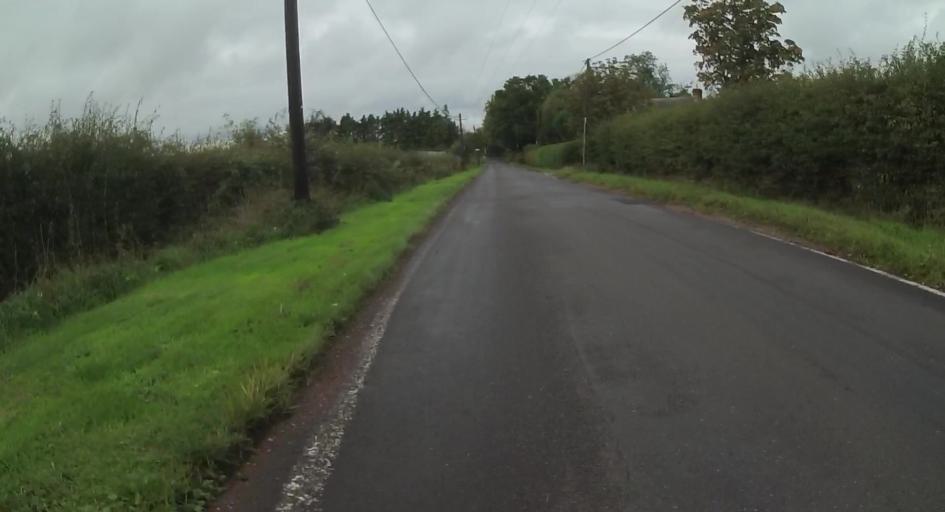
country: GB
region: England
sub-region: Hampshire
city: Tadley
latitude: 51.3155
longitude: -1.1598
